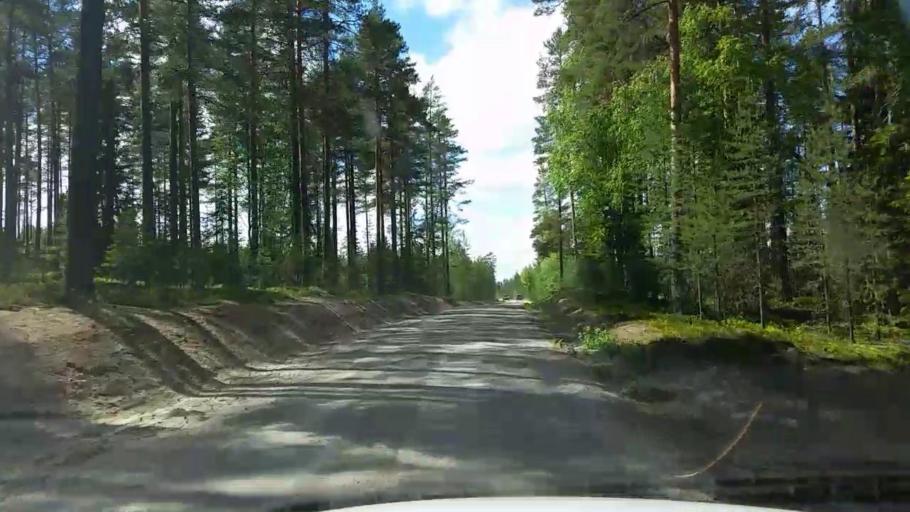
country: SE
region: Gaevleborg
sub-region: Ovanakers Kommun
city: Edsbyn
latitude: 61.5715
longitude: 15.9351
